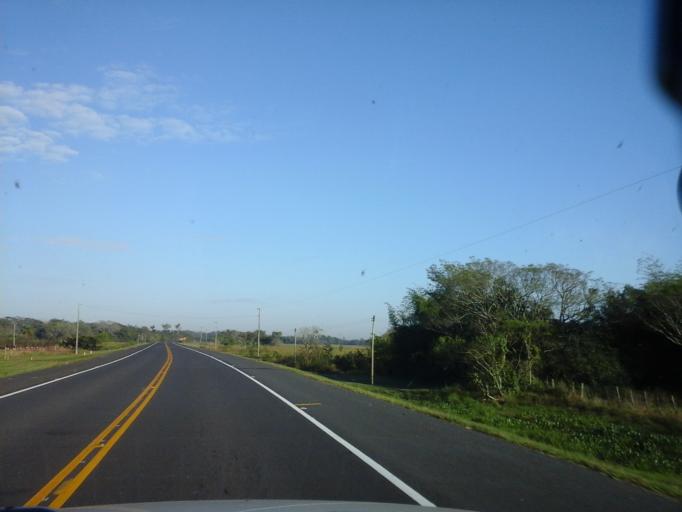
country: PY
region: Neembucu
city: Pilar
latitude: -26.8742
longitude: -57.9036
